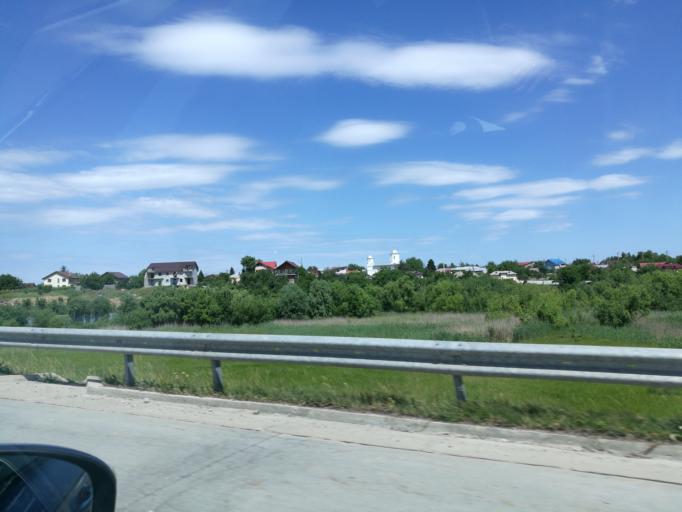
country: RO
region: Ilfov
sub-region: Comuna Cernica
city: Caldararu
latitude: 44.4087
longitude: 26.2629
